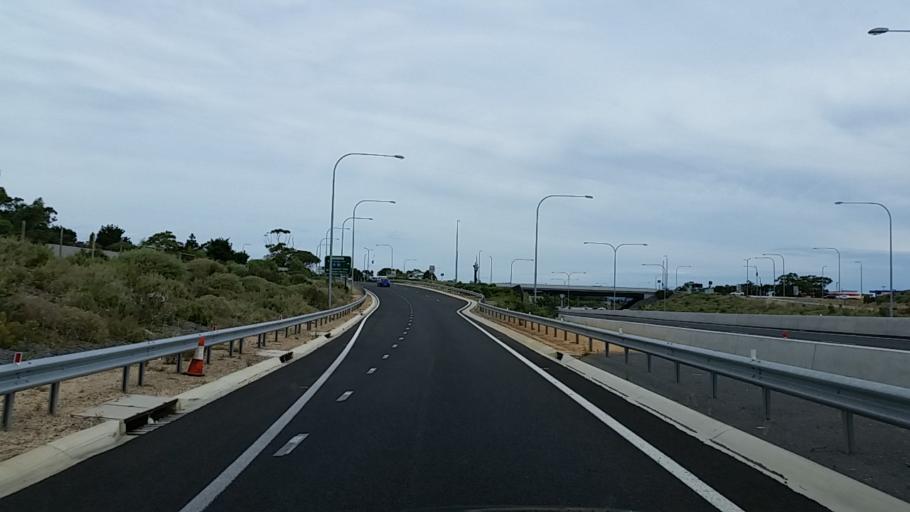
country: AU
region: South Australia
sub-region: Onkaparinga
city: Morphett Vale
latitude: -35.1351
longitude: 138.5057
